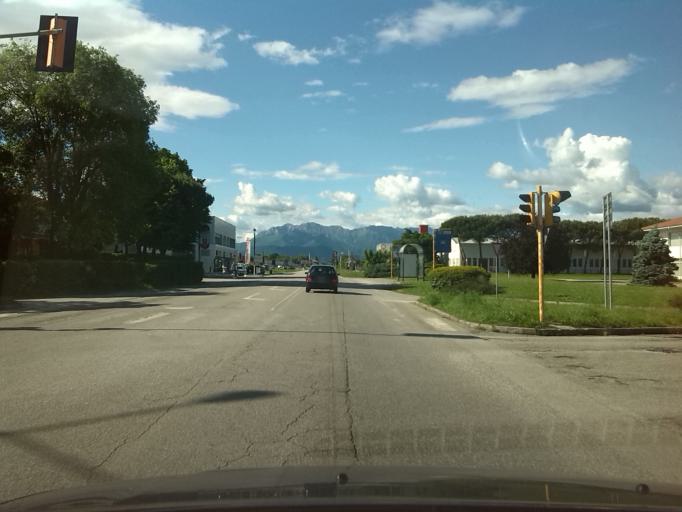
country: IT
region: Friuli Venezia Giulia
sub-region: Provincia di Udine
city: Tavagnacco
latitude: 46.1074
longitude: 13.2288
